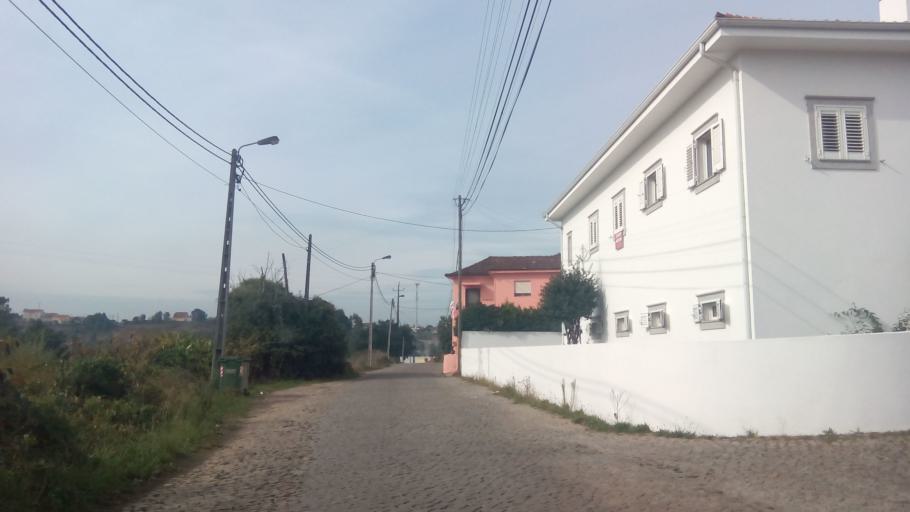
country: PT
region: Porto
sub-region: Paredes
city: Gandra
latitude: 41.1863
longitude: -8.4305
